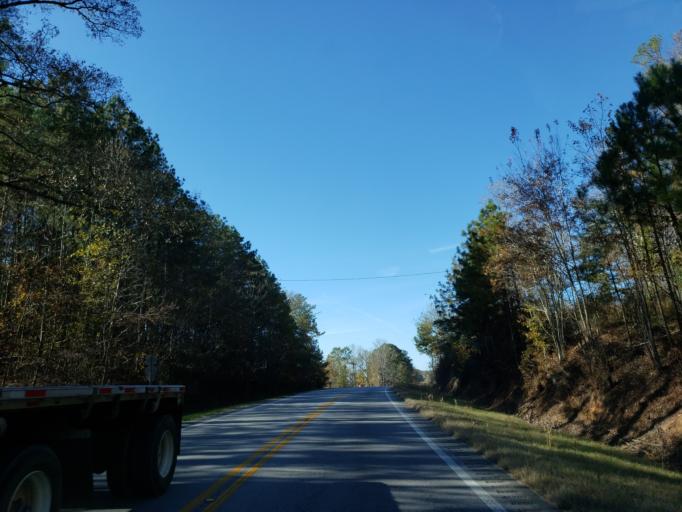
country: US
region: Alabama
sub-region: Calhoun County
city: Choccolocco
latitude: 33.5566
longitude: -85.6571
